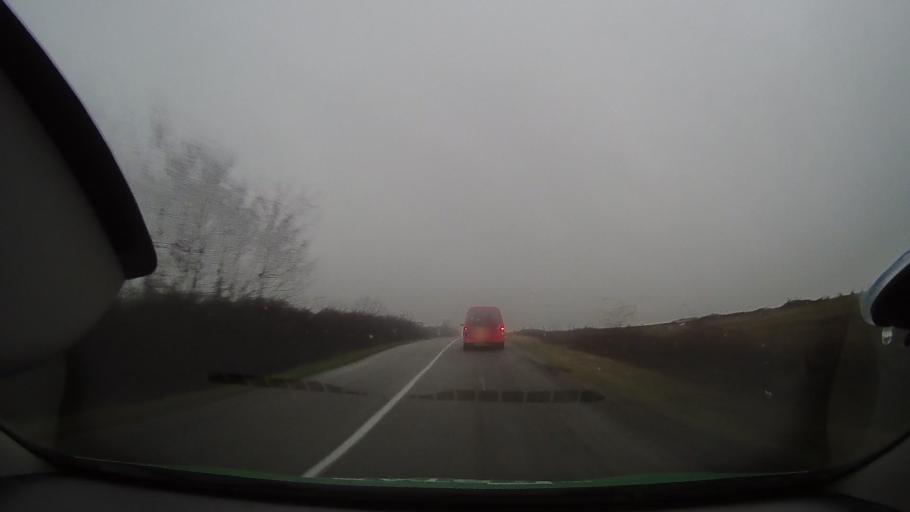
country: RO
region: Arad
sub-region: Comuna Craiova
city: Craiova
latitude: 46.6154
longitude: 21.9570
